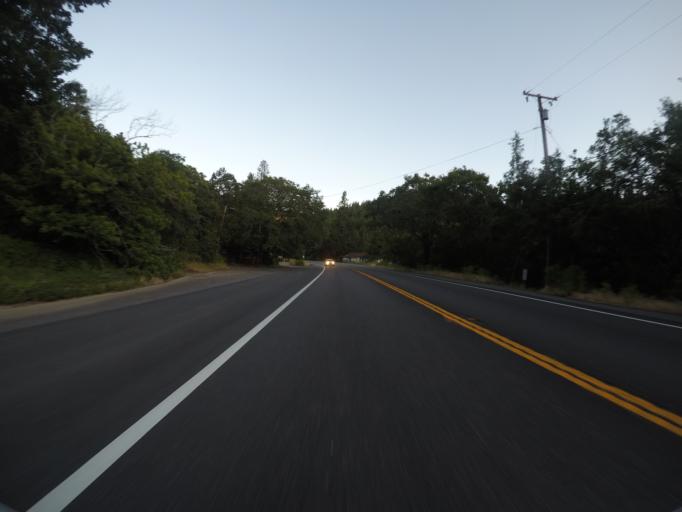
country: US
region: California
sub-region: Humboldt County
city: Redway
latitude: 39.8885
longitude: -123.7478
